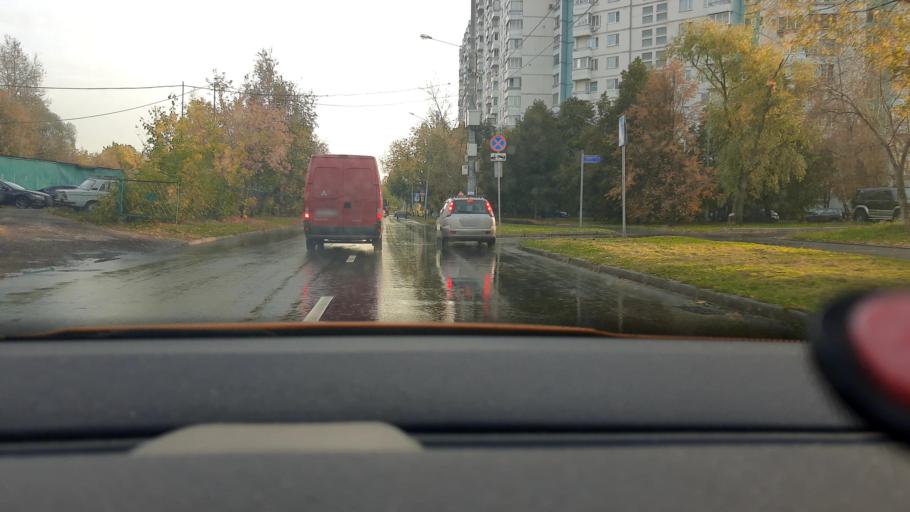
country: RU
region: Moscow
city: Gol'yanovo
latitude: 55.8179
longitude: 37.8352
